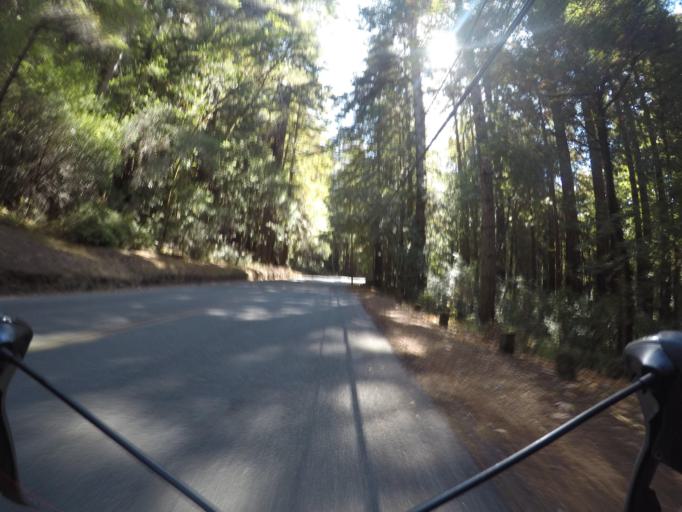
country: US
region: California
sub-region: San Mateo County
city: Portola Valley
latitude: 37.2782
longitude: -122.2939
